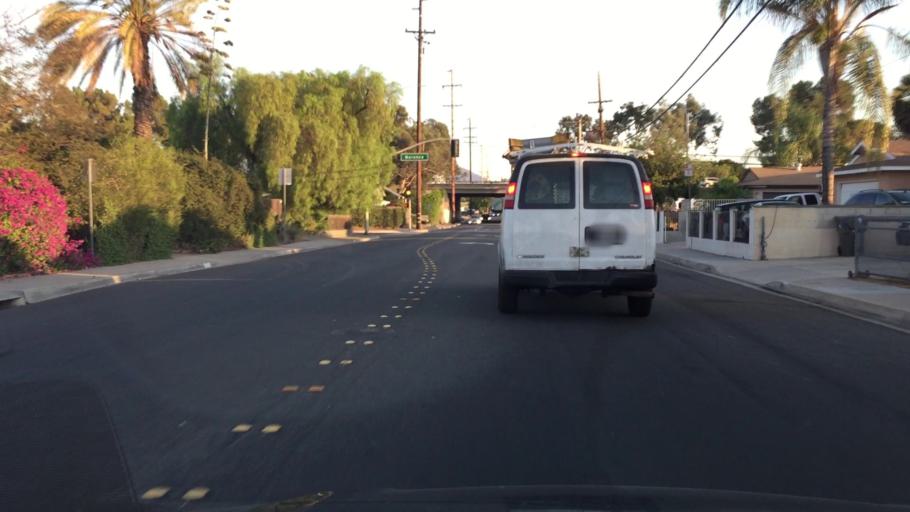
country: US
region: California
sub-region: San Diego County
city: Bostonia
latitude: 32.8047
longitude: -116.9446
